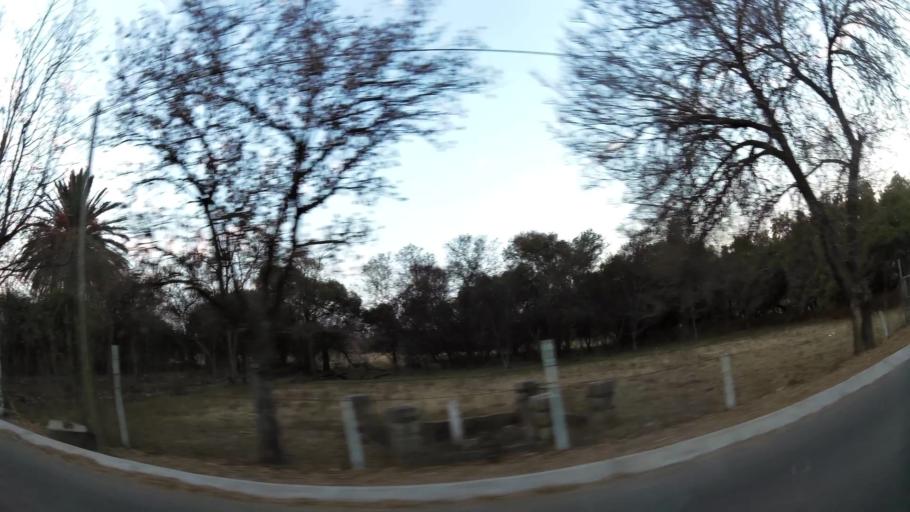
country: ZA
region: Gauteng
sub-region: City of Johannesburg Metropolitan Municipality
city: Midrand
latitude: -26.0088
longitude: 28.0482
